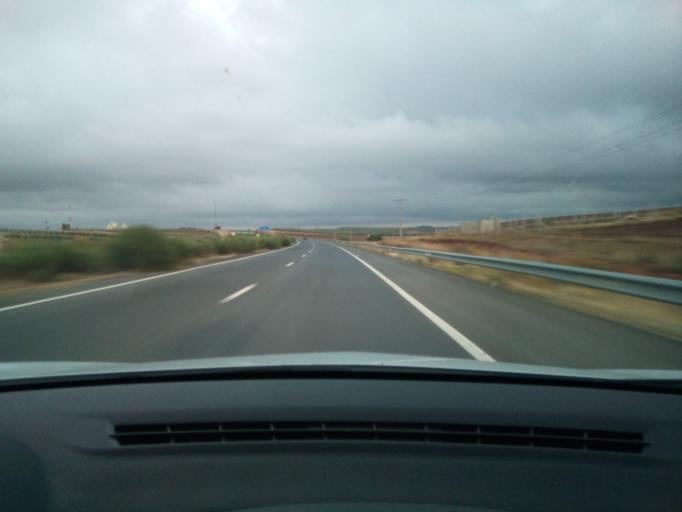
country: MA
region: Meknes-Tafilalet
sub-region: Meknes
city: Meknes
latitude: 33.8475
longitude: -5.6177
